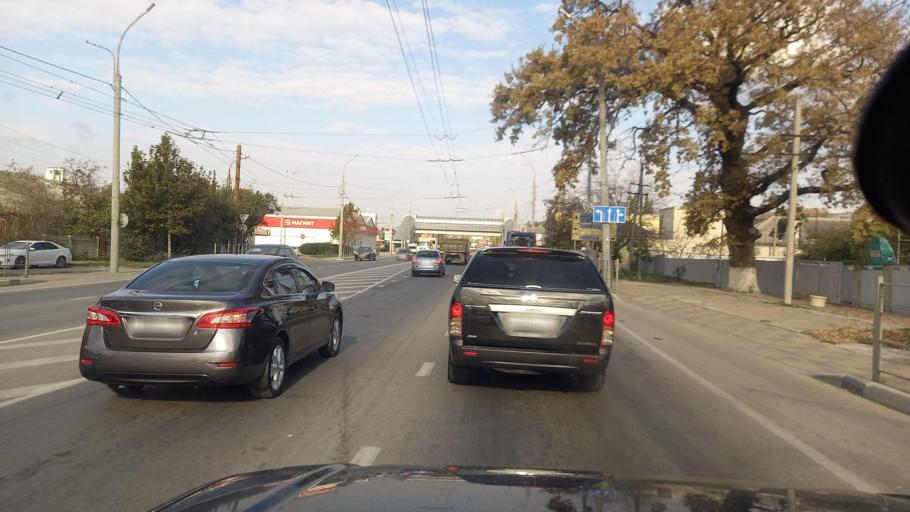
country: RU
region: Krasnodarskiy
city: Gayduk
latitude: 44.7606
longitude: 37.7212
